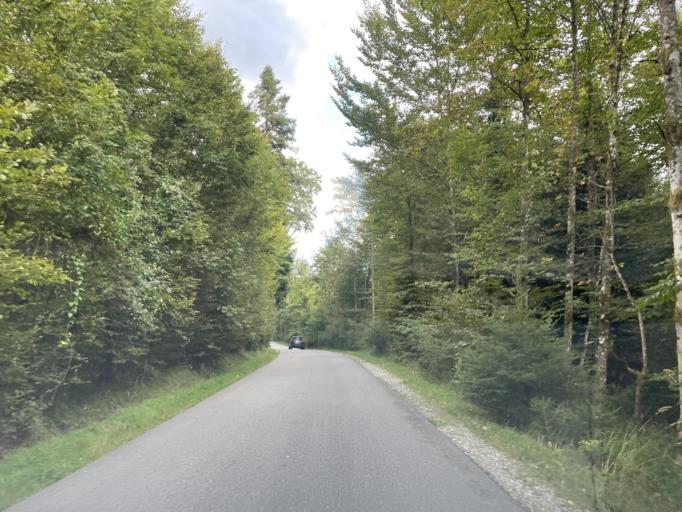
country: CH
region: Zurich
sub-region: Bezirk Winterthur
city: Mattenbach (Kreis 7)
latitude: 47.4762
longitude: 8.7346
